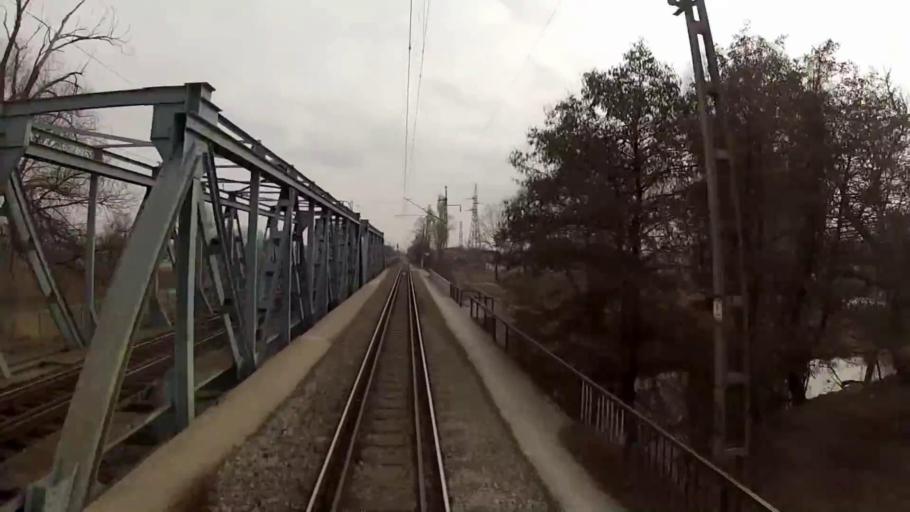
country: BG
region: Sofiya
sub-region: Obshtina Elin Pelin
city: Elin Pelin
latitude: 42.6531
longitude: 23.4659
